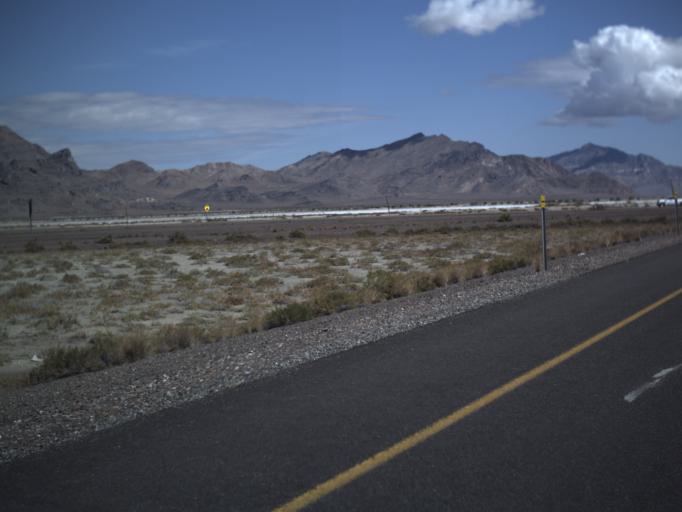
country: US
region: Utah
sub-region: Tooele County
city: Wendover
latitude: 40.7405
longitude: -113.9684
